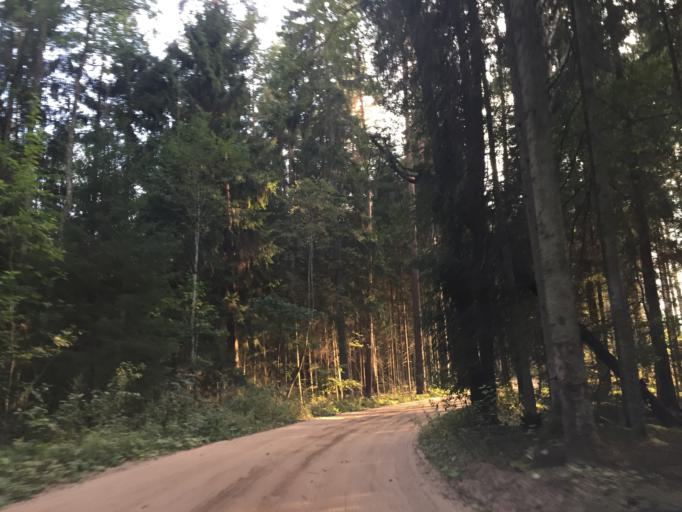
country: LV
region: Baldone
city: Baldone
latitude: 56.7604
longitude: 24.4101
